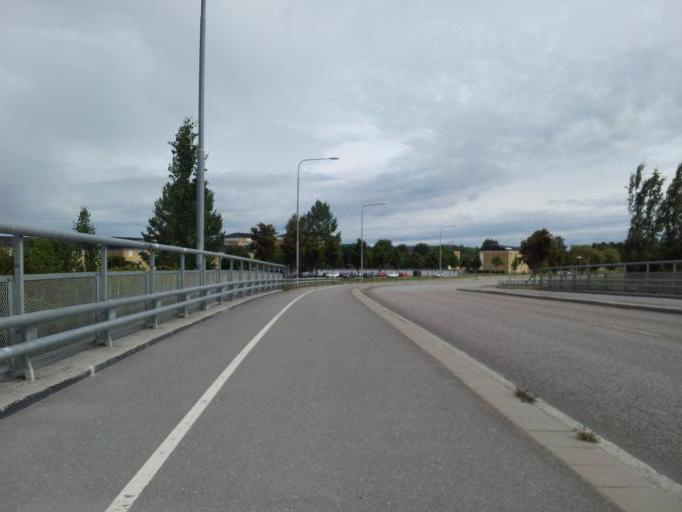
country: SE
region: Uppsala
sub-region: Uppsala Kommun
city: Gamla Uppsala
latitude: 59.8840
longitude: 17.6554
